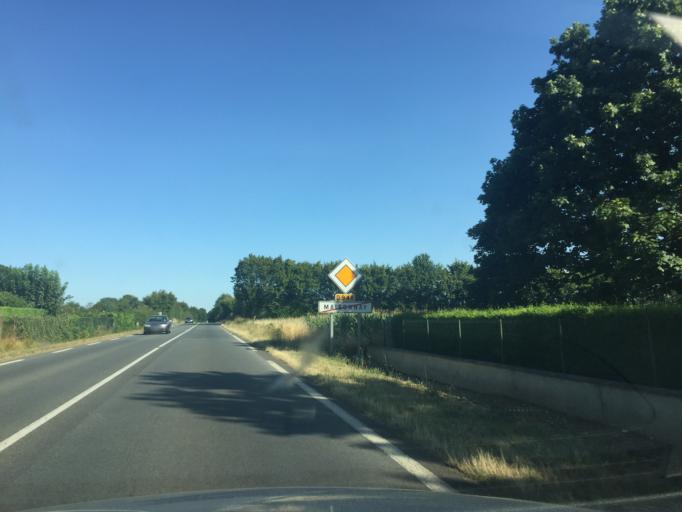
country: FR
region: Poitou-Charentes
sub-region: Departement des Deux-Sevres
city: Chef-Boutonne
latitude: 46.1889
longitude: -0.0493
